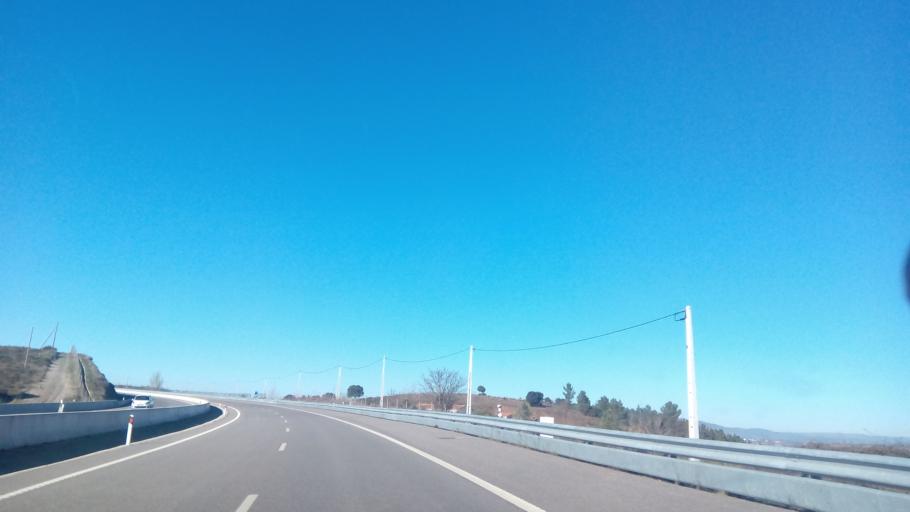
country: PT
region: Braganca
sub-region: Braganca Municipality
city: Braganca
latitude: 41.7884
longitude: -6.7094
